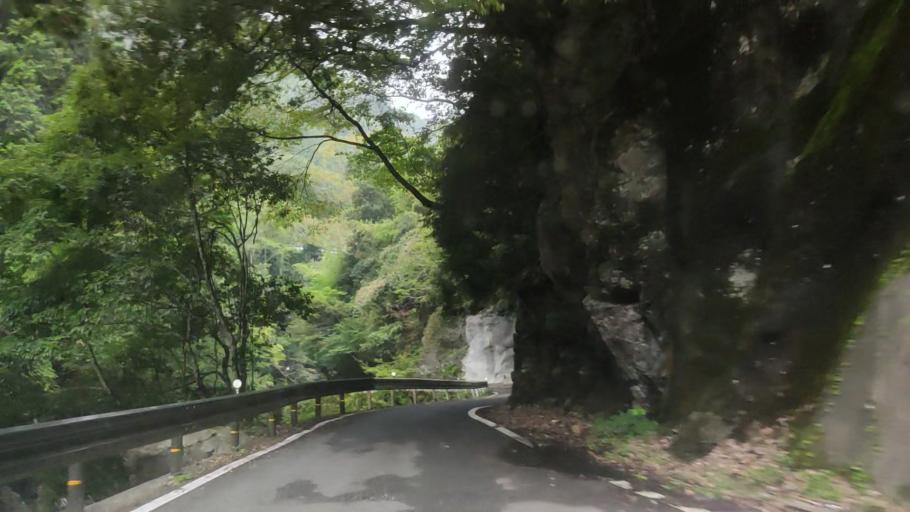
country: JP
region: Wakayama
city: Koya
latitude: 34.2563
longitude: 135.6520
